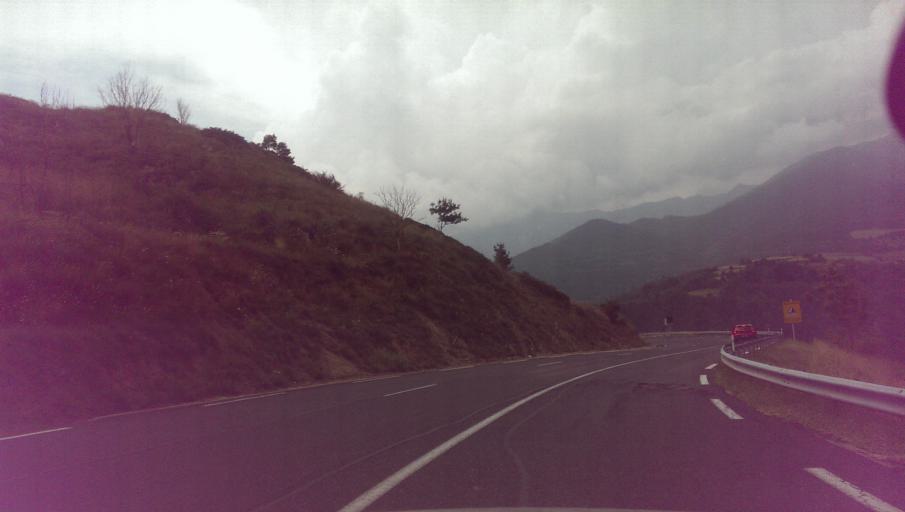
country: ES
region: Catalonia
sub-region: Provincia de Girona
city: Llivia
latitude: 42.5069
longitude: 2.1339
